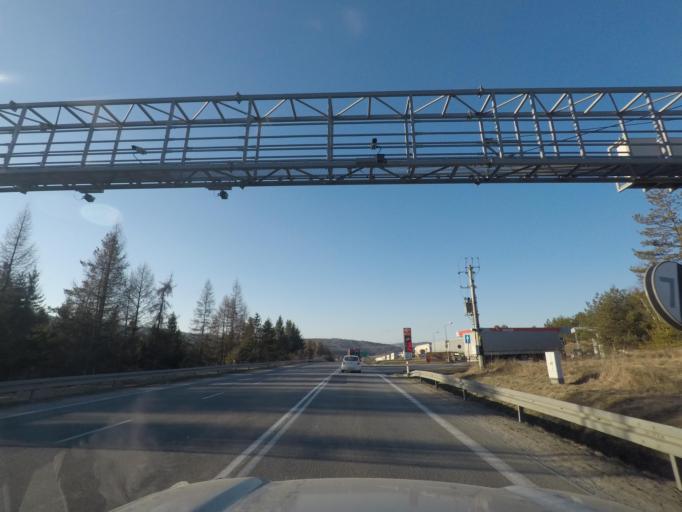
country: PL
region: Subcarpathian Voivodeship
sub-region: Powiat krosnienski
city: Jasliska
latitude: 49.4234
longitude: 21.6927
